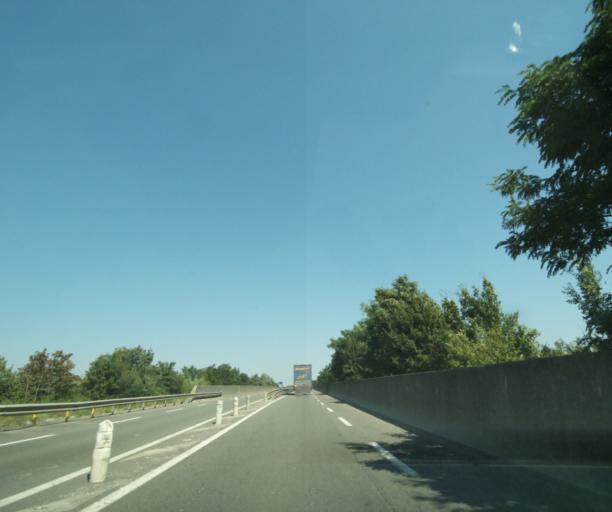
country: FR
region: Champagne-Ardenne
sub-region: Departement de la Haute-Marne
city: Saint-Dizier
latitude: 48.6342
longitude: 4.9238
